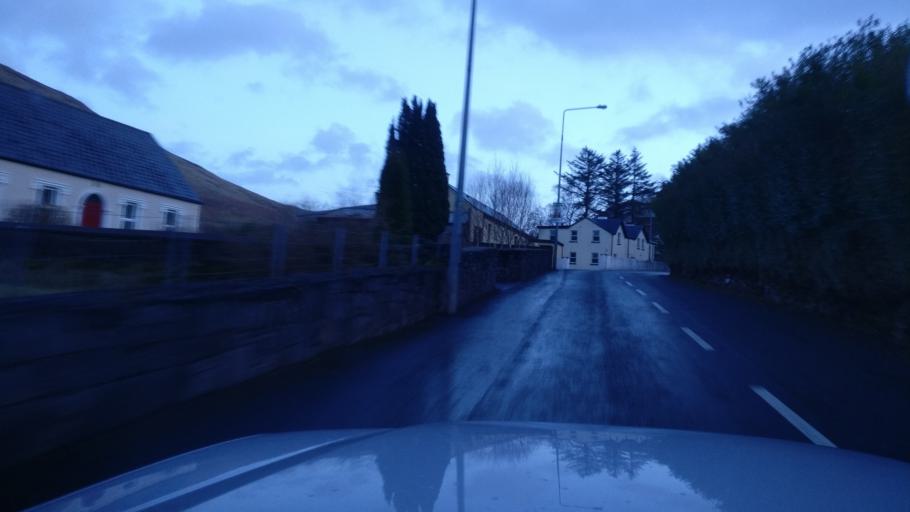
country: IE
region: Connaught
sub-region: Maigh Eo
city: Westport
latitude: 53.5947
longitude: -9.6921
